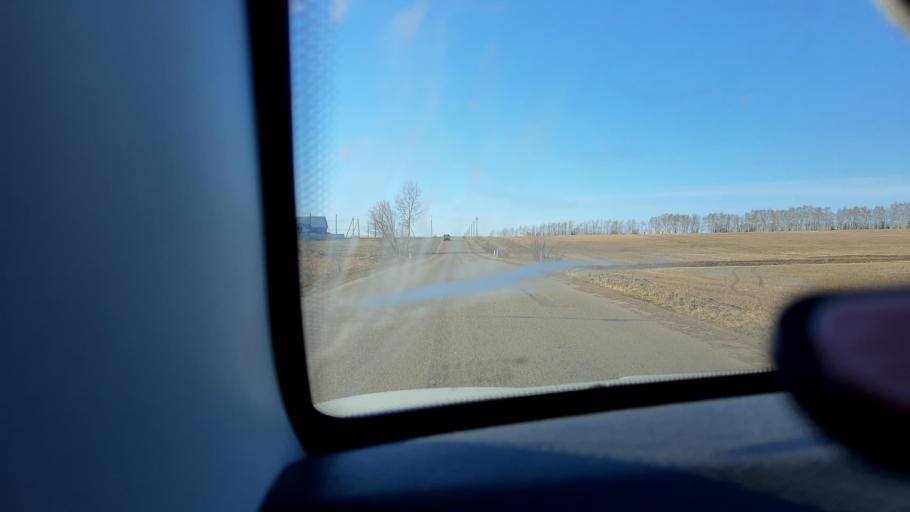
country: RU
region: Bashkortostan
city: Asanovo
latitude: 54.8310
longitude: 55.4634
